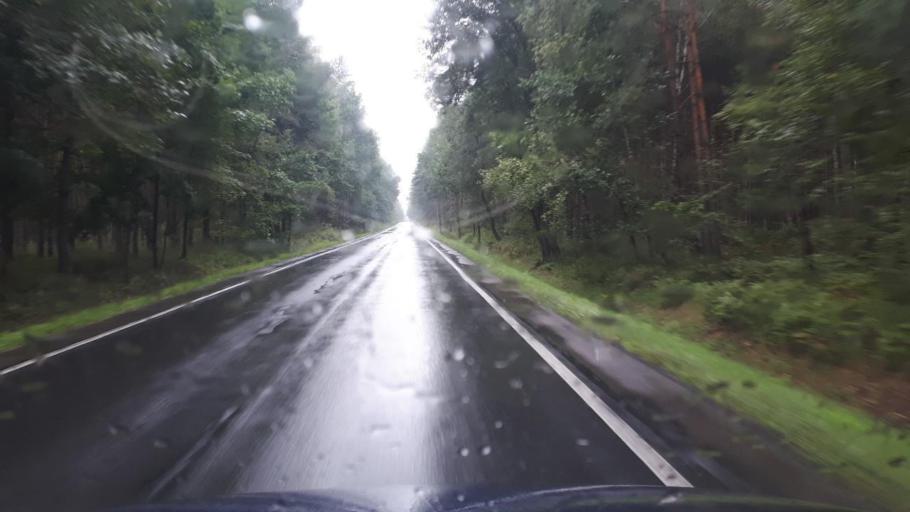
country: PL
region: Silesian Voivodeship
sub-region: Powiat tarnogorski
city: Tworog
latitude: 50.5304
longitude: 18.6918
